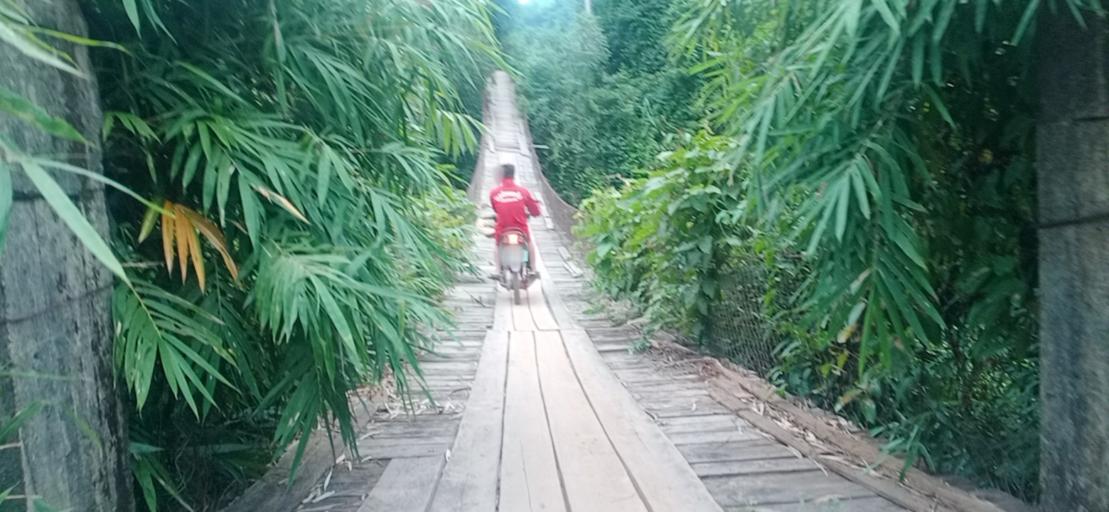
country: TH
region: Changwat Bueng Kan
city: Pak Khat
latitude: 18.5597
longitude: 103.2410
